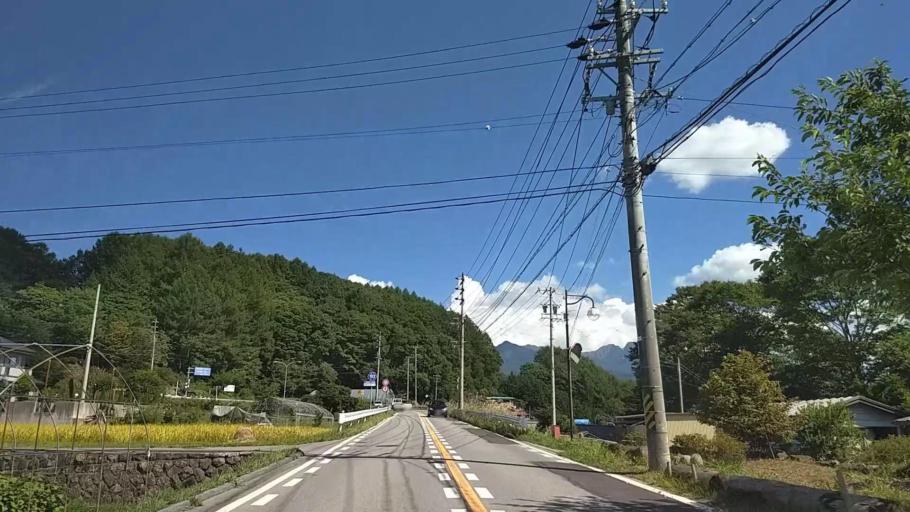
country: JP
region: Nagano
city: Chino
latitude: 36.0323
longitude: 138.2296
